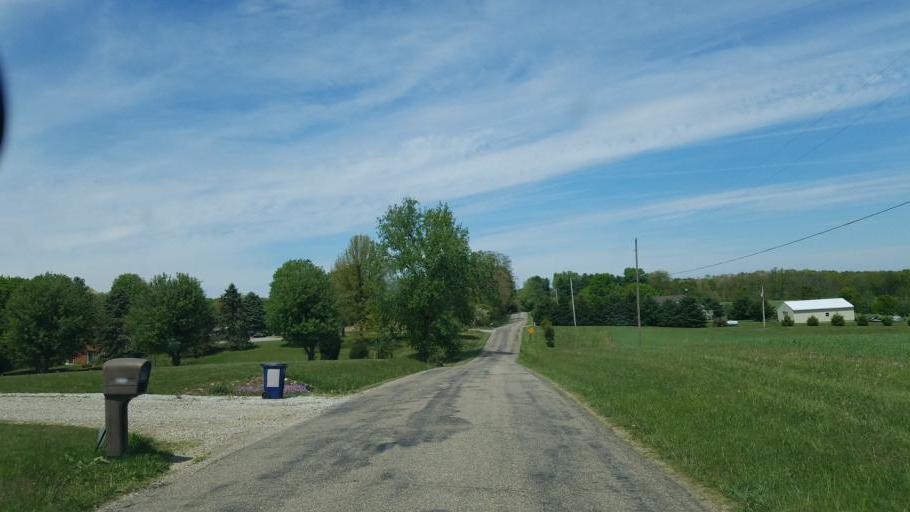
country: US
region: Ohio
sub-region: Knox County
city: Gambier
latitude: 40.4023
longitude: -82.4069
